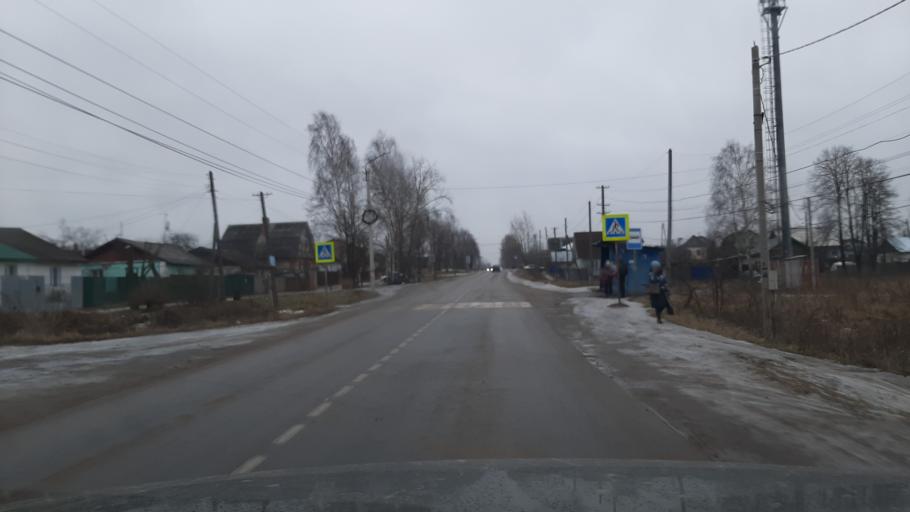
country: RU
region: Ivanovo
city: Shuya
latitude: 56.8743
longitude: 41.3513
